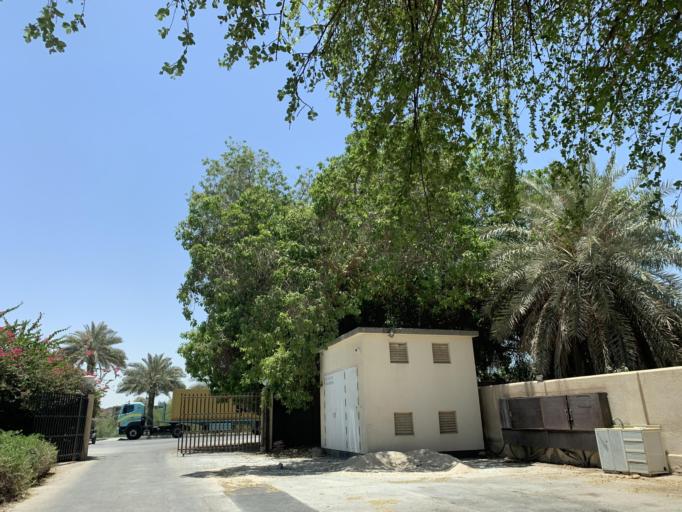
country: BH
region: Manama
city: Jidd Hafs
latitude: 26.2225
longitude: 50.4794
